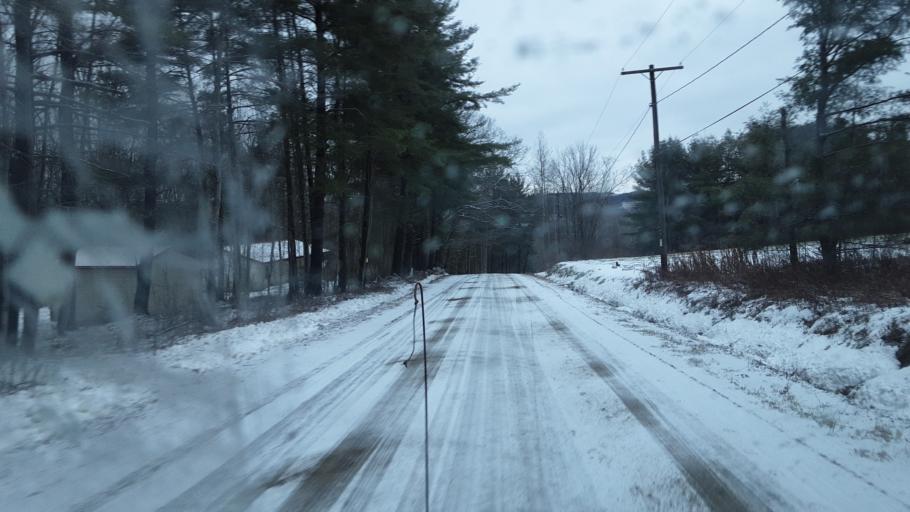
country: US
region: New York
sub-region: Allegany County
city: Friendship
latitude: 42.2855
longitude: -78.1617
